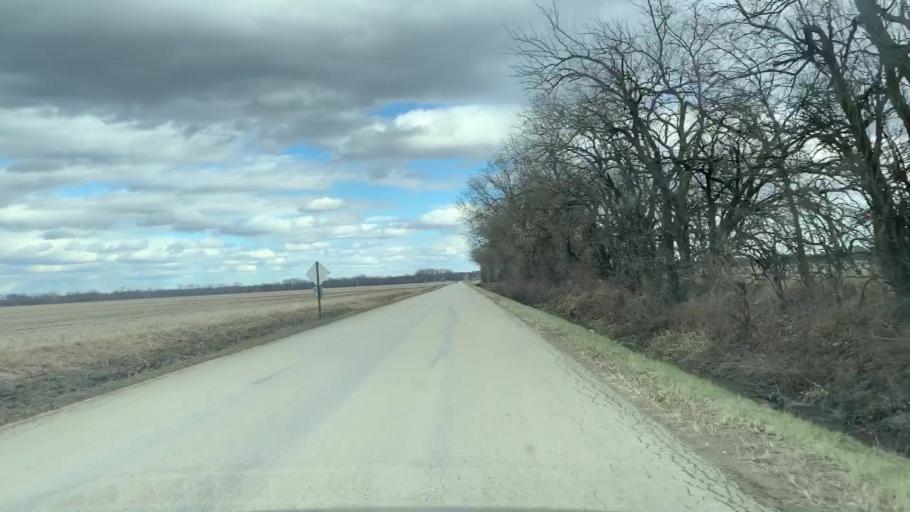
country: US
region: Kansas
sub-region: Allen County
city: Humboldt
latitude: 37.8130
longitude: -95.4693
